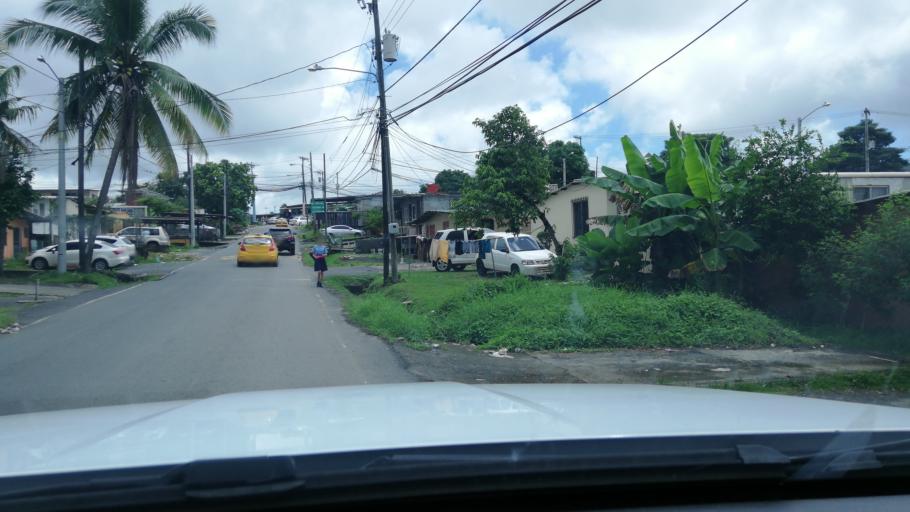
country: PA
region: Panama
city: Tocumen
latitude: 9.1046
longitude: -79.3649
